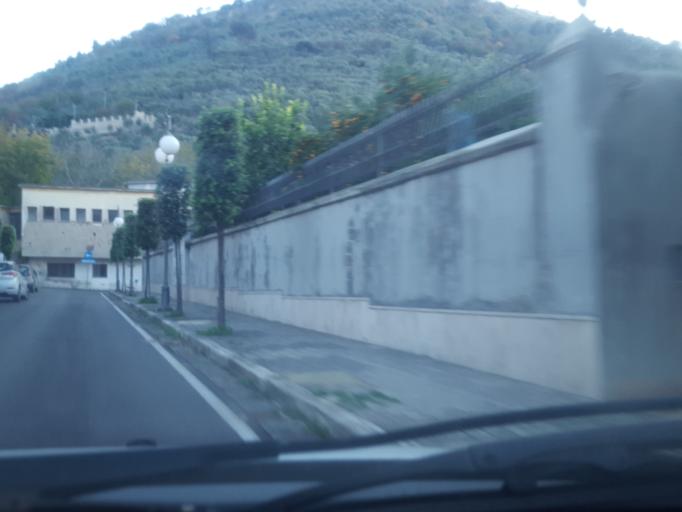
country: IT
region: Campania
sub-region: Provincia di Caserta
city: Arienzo
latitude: 41.0221
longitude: 14.4986
